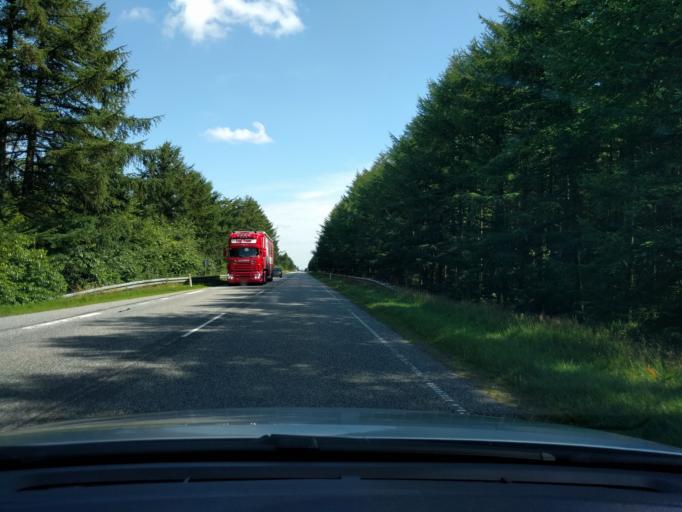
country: DK
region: Central Jutland
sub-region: Herning Kommune
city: Kibaek
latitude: 56.0545
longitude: 8.8886
